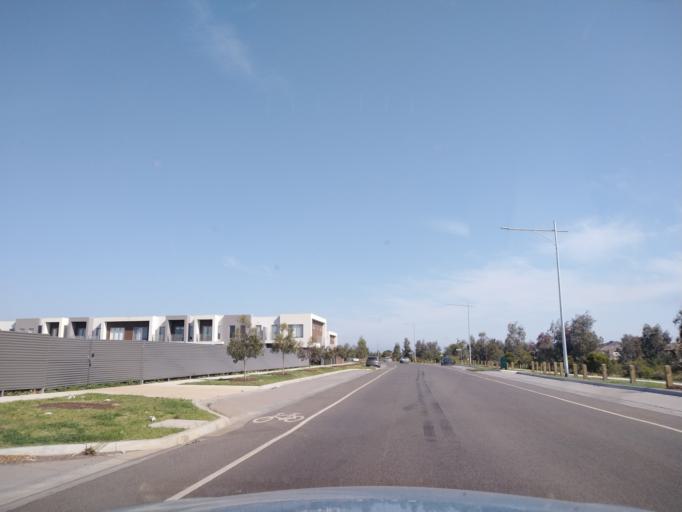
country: AU
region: Victoria
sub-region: Wyndham
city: Williams Landing
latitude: -37.8447
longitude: 144.7403
